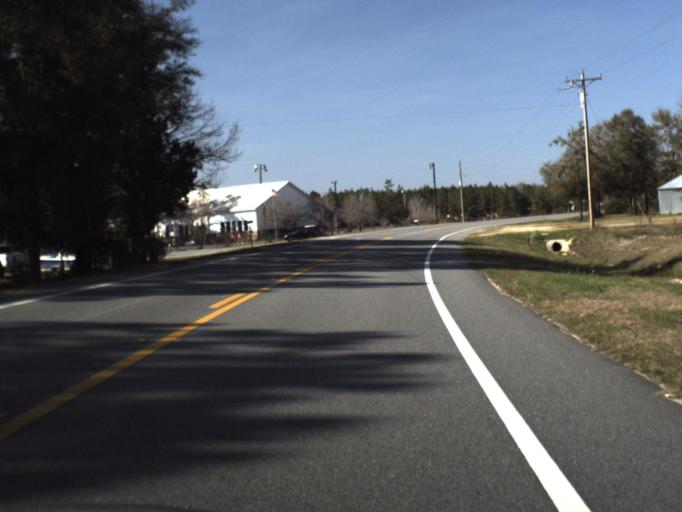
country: US
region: Florida
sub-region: Gulf County
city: Wewahitchka
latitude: 30.2645
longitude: -85.2413
